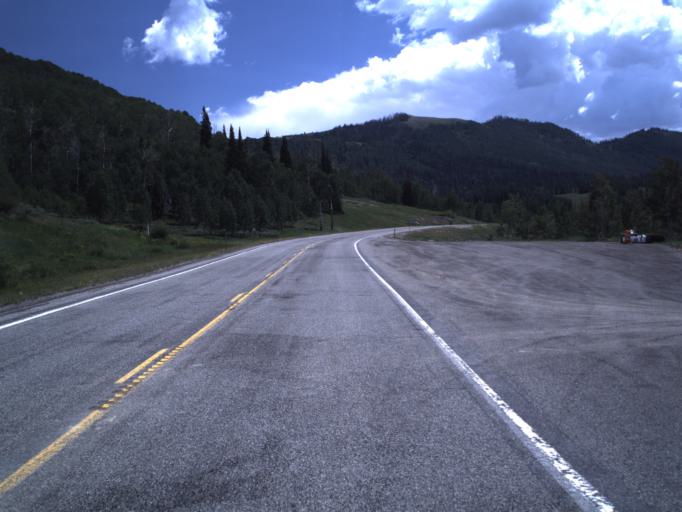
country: US
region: Utah
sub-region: Sanpete County
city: Fairview
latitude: 39.5867
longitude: -111.2399
